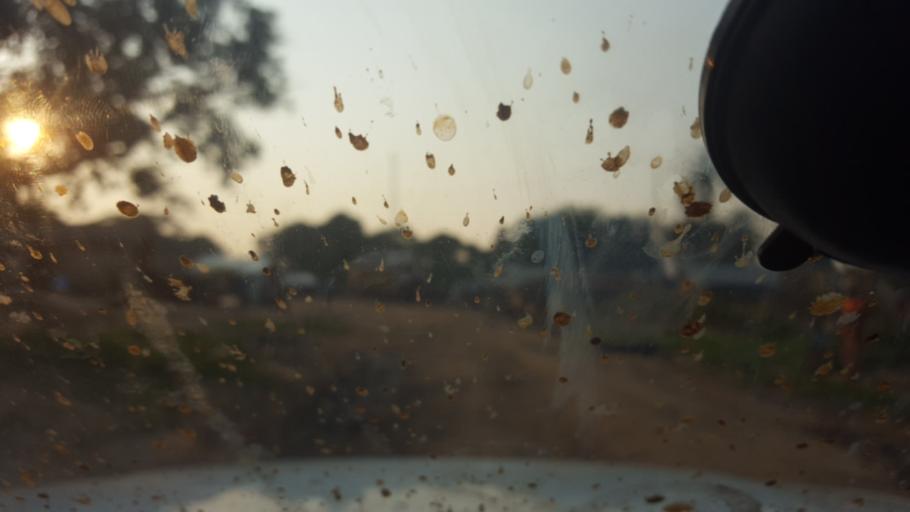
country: CD
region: Bandundu
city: Mushie
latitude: -3.7419
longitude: 16.6525
